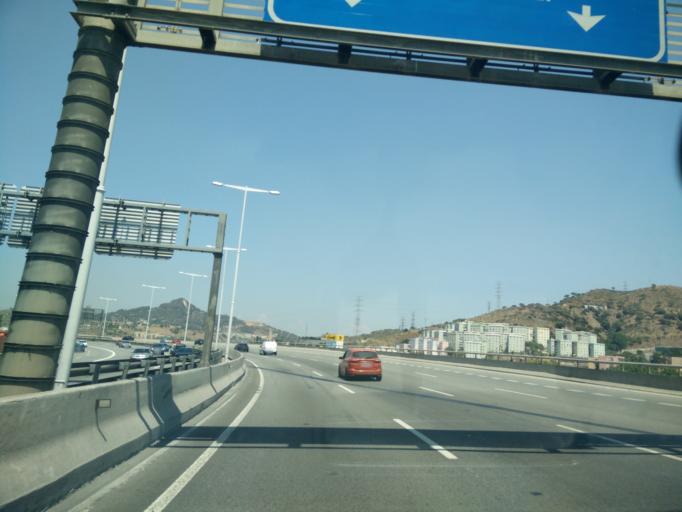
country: ES
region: Catalonia
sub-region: Provincia de Barcelona
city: Santa Coloma de Gramenet
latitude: 41.4534
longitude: 2.1950
